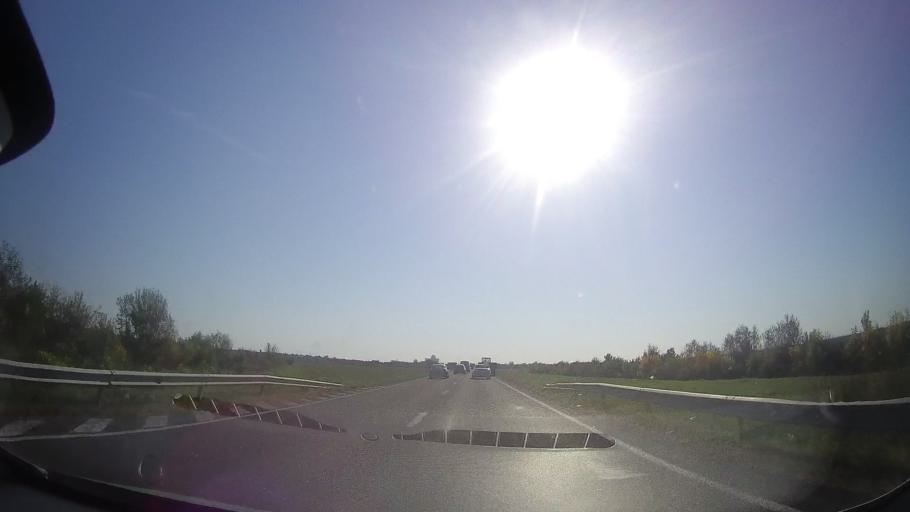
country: RO
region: Timis
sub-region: Comuna Topolovatu Mare
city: Topolovatu Mare
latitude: 45.7813
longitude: 21.6049
